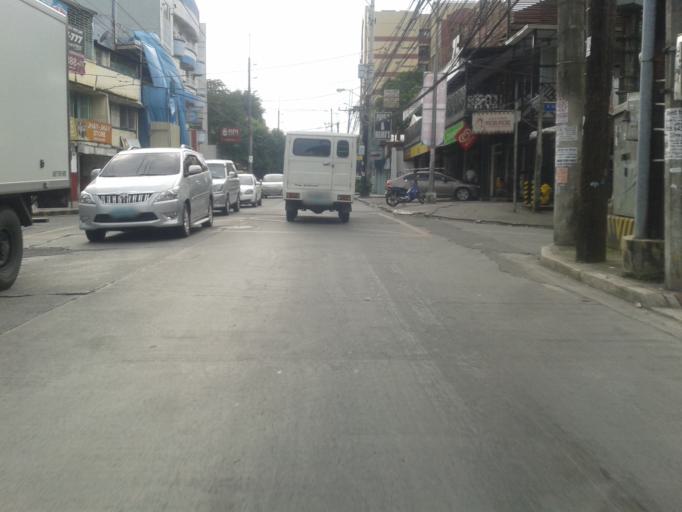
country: PH
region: Metro Manila
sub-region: Marikina
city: Calumpang
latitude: 14.6348
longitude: 121.0709
